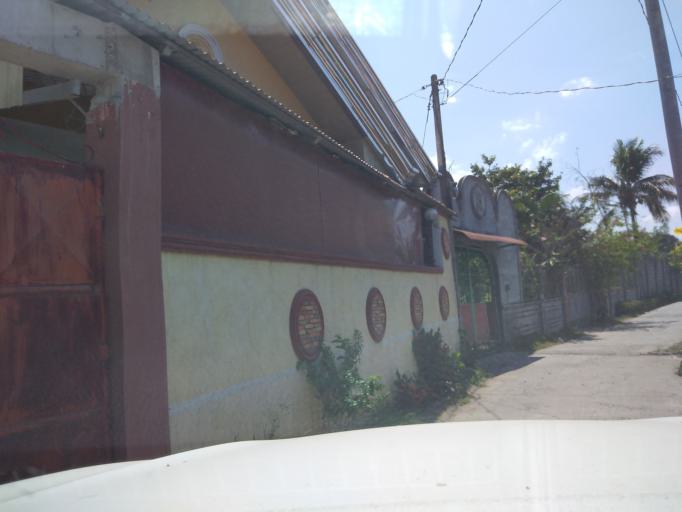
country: PH
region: Central Luzon
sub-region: Province of Pampanga
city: Lourdes
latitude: 15.0185
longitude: 120.8527
